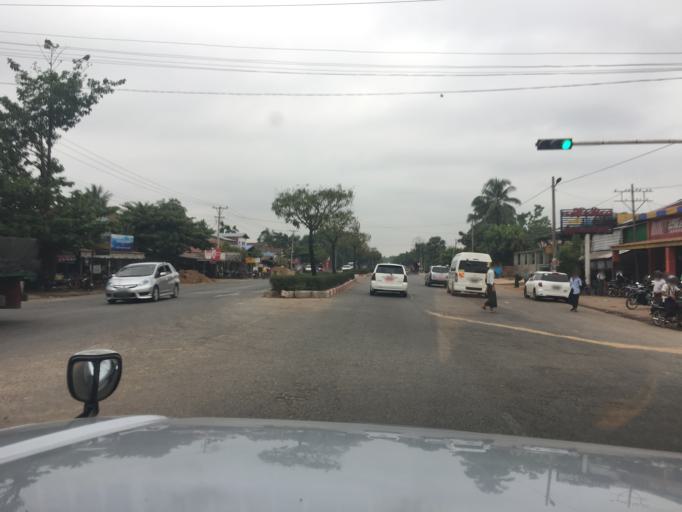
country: MM
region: Bago
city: Thanatpin
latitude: 17.1853
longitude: 96.3853
